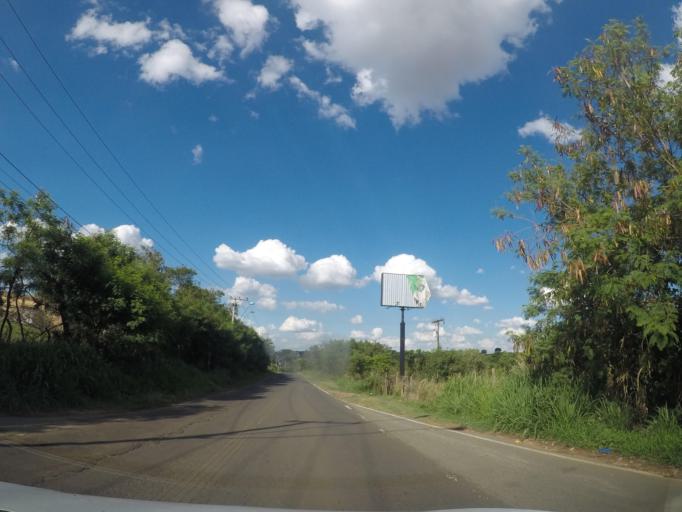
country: BR
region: Sao Paulo
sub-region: Sumare
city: Sumare
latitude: -22.8558
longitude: -47.2891
